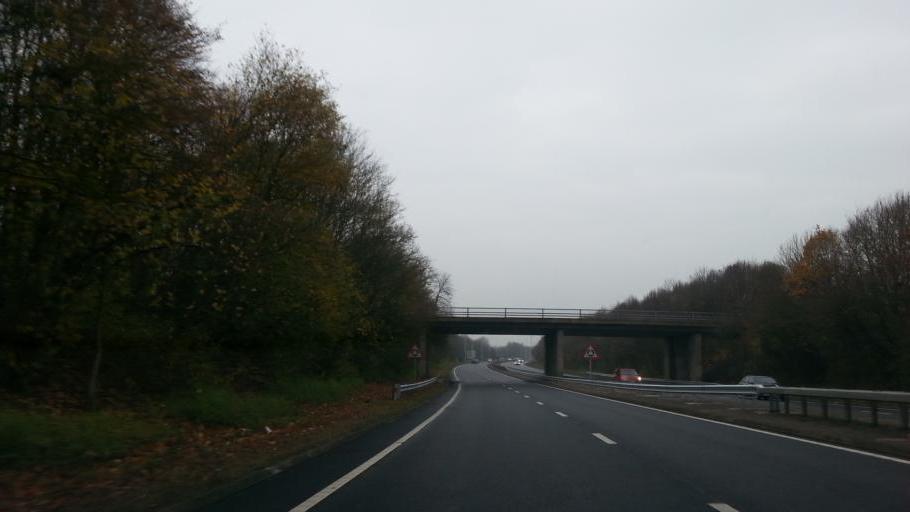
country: GB
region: England
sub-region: Cambridgeshire
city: Yaxley
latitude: 52.5409
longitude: -0.3044
